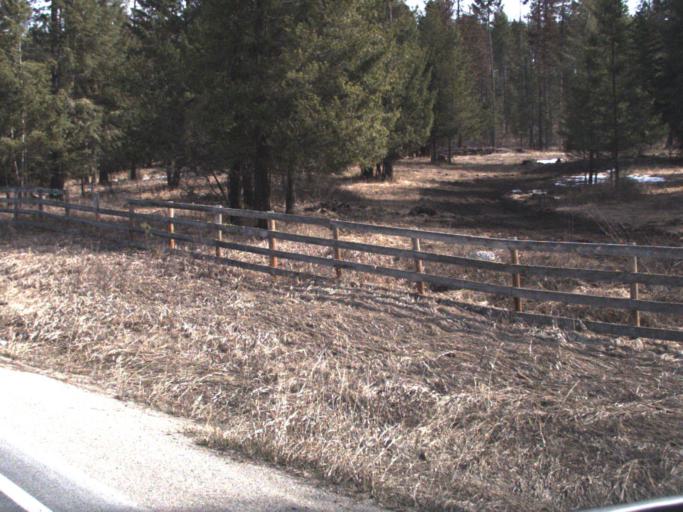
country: US
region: Washington
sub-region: Stevens County
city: Colville
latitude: 48.5118
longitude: -117.7004
